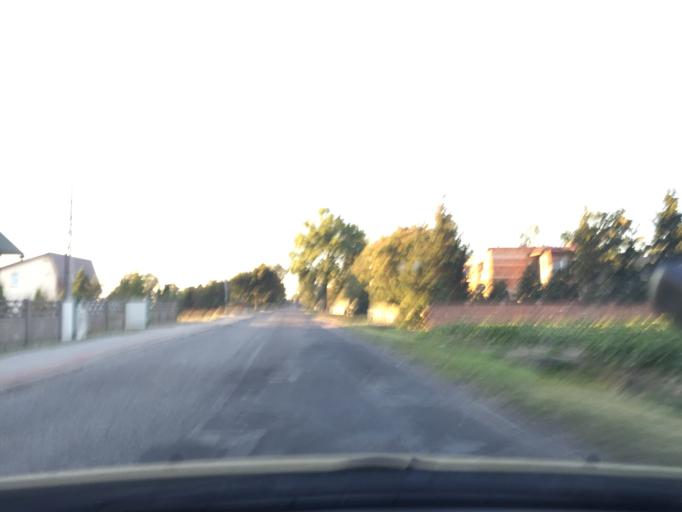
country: PL
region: Greater Poland Voivodeship
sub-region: Powiat pleszewski
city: Dobrzyca
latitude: 51.8142
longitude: 17.6220
